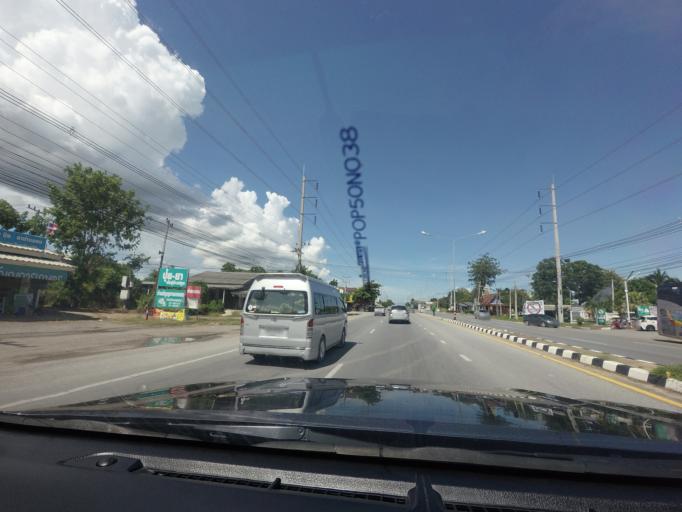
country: TH
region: Kanchanaburi
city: Phanom Thuan
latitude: 14.0752
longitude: 99.6541
